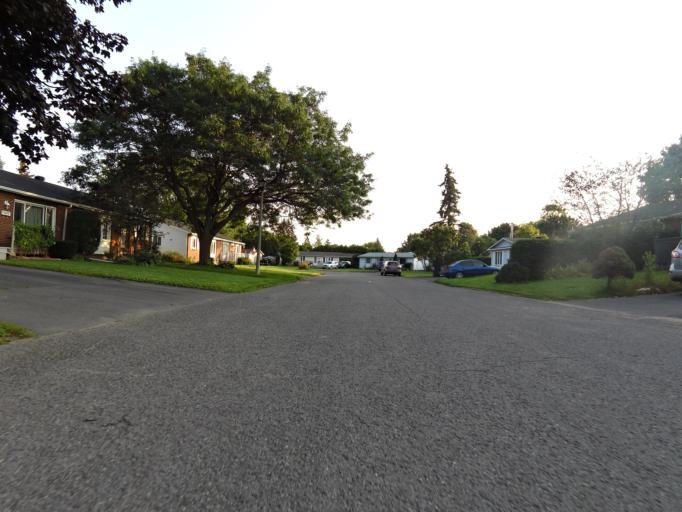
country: CA
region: Ontario
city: Bells Corners
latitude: 45.2901
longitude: -75.8821
